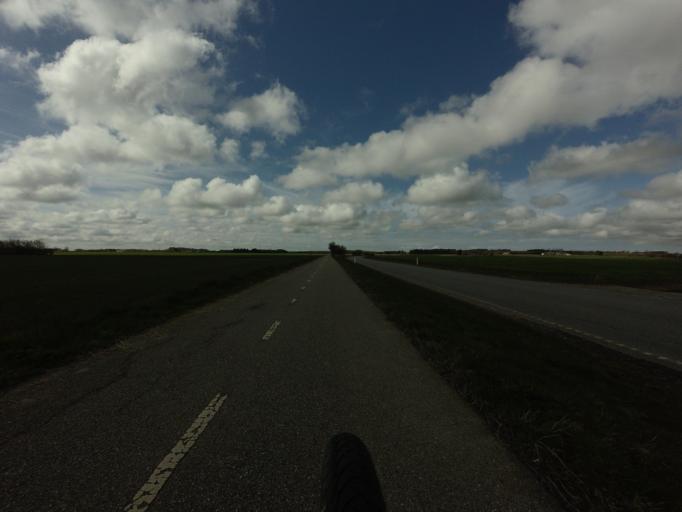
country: DK
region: North Denmark
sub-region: Hjorring Kommune
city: Vra
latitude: 57.3530
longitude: 9.9029
